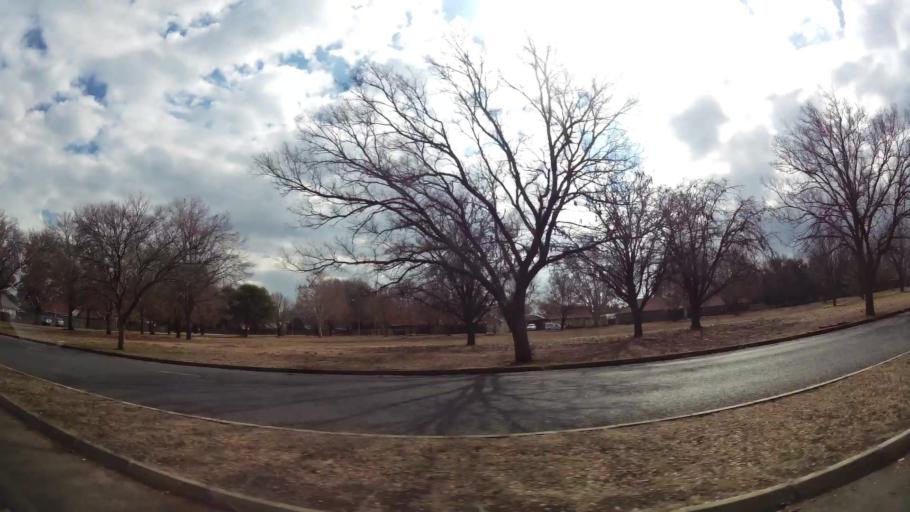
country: ZA
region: Gauteng
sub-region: Sedibeng District Municipality
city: Vereeniging
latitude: -26.6588
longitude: 27.9876
